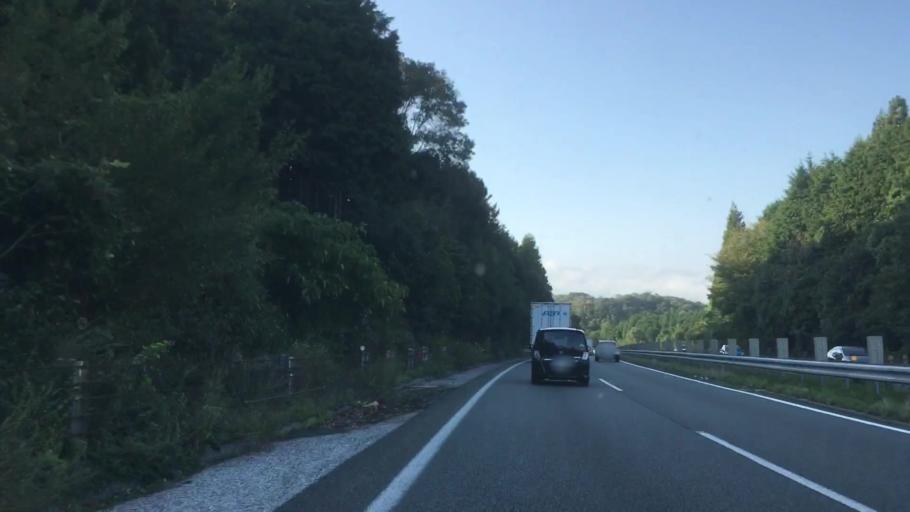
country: JP
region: Yamaguchi
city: Ogori-shimogo
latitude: 34.1566
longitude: 131.3329
